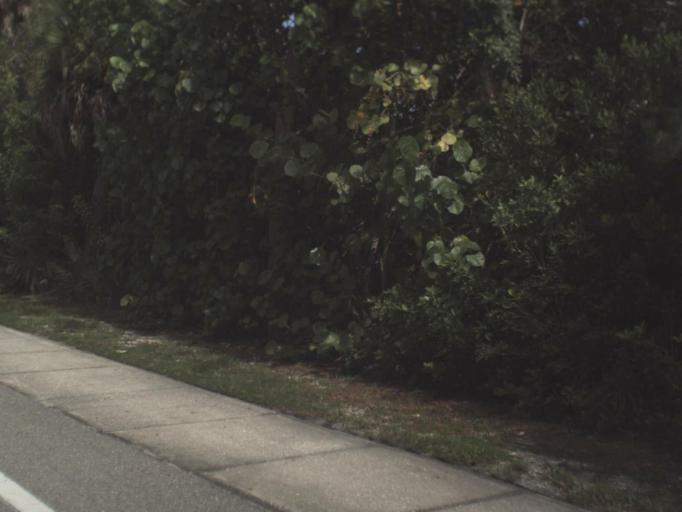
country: US
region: Florida
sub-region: Sarasota County
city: Siesta Key
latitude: 27.2827
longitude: -82.5535
